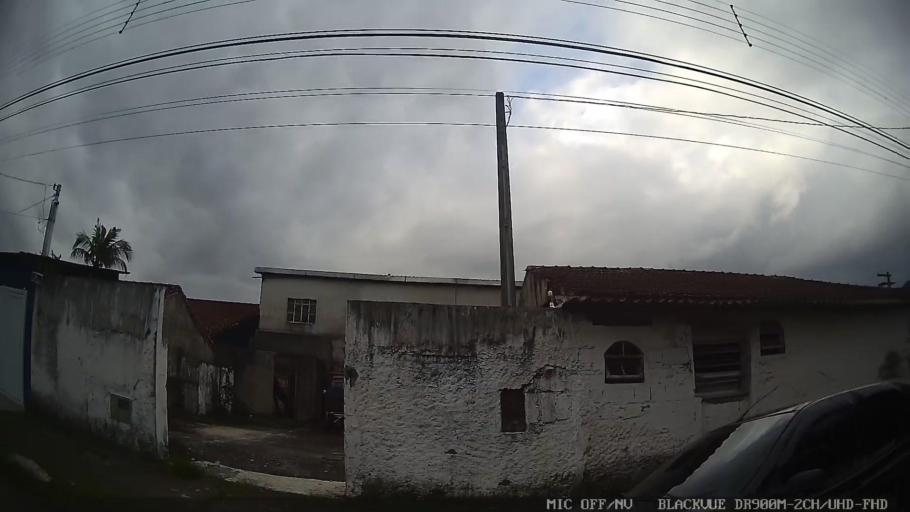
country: BR
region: Sao Paulo
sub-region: Guaruja
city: Guaruja
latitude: -23.9969
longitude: -46.2771
